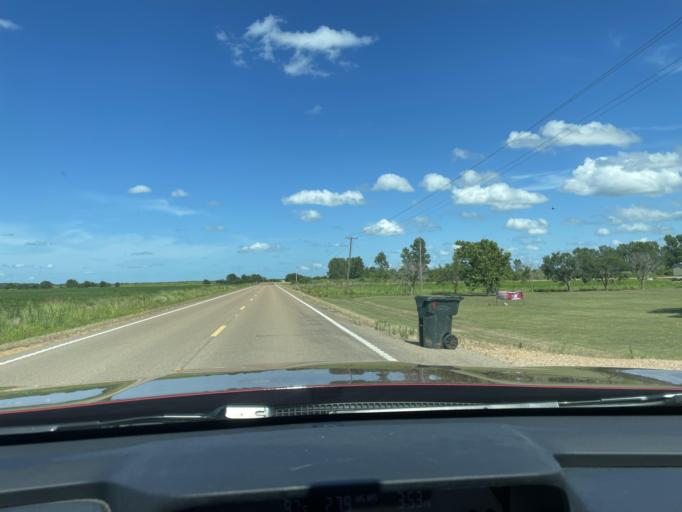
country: US
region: Mississippi
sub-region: Humphreys County
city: Belzoni
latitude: 33.1843
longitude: -90.6670
